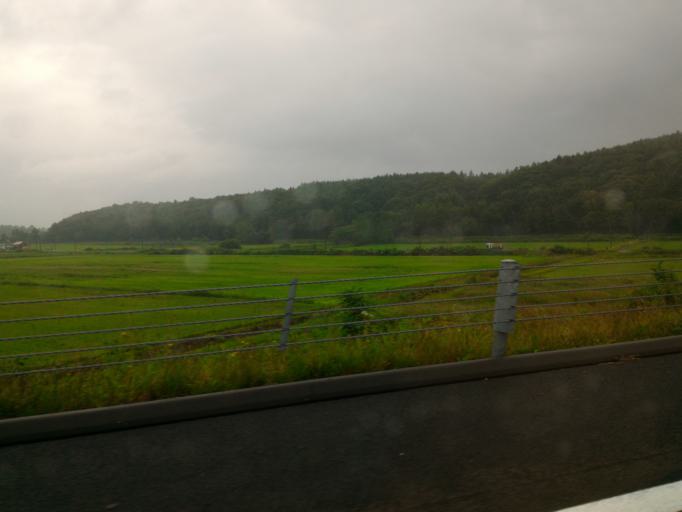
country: JP
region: Hokkaido
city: Nayoro
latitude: 44.4936
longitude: 142.3531
